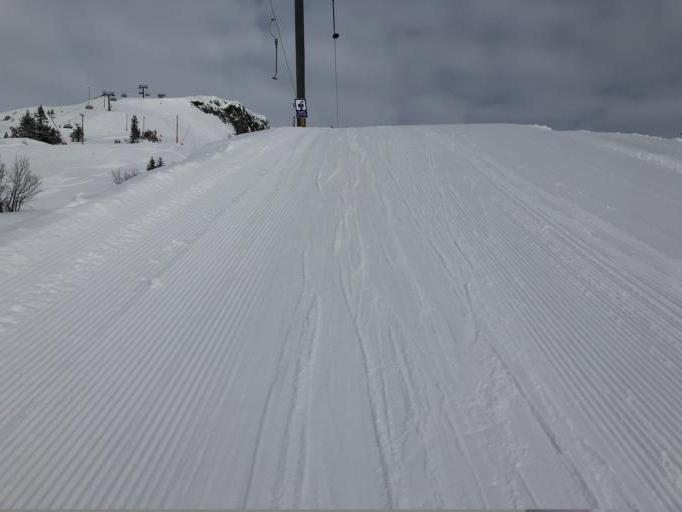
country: NO
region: Oppland
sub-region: Gausdal
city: Segalstad bru
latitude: 61.3428
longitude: 10.0880
